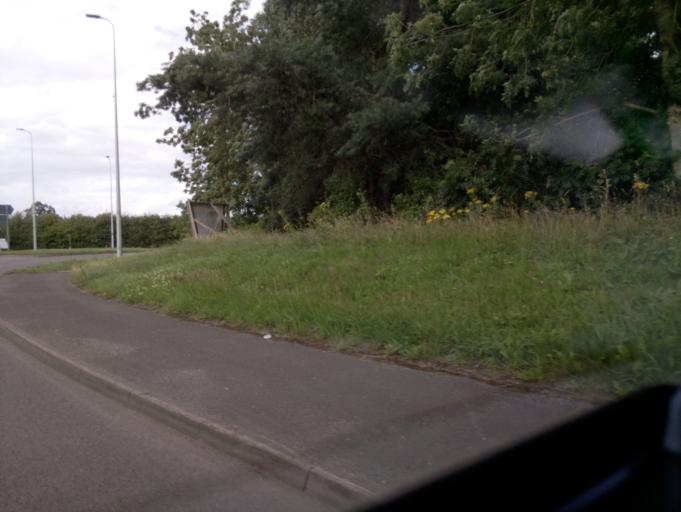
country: GB
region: England
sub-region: Leicestershire
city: Donisthorpe
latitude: 52.6887
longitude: -1.5470
